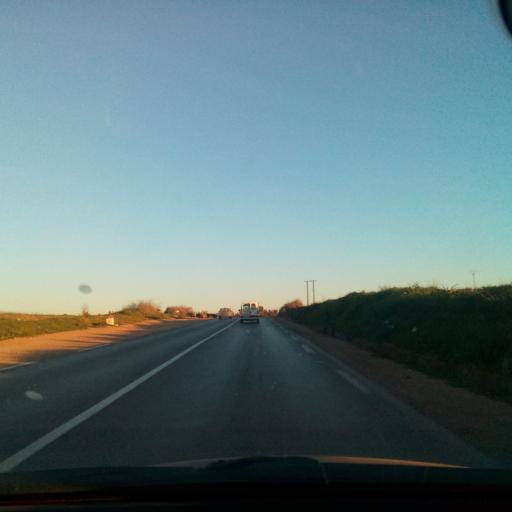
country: DZ
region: Relizane
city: Relizane
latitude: 35.7355
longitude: 0.2973
